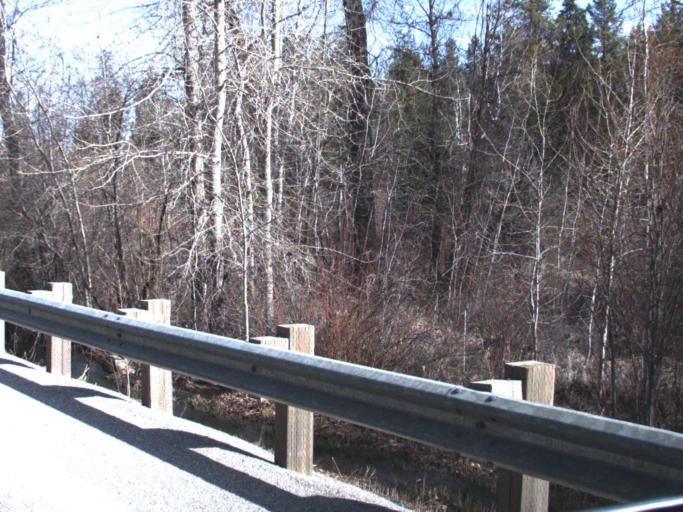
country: US
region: Washington
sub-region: Stevens County
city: Colville
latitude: 48.5378
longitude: -117.8240
